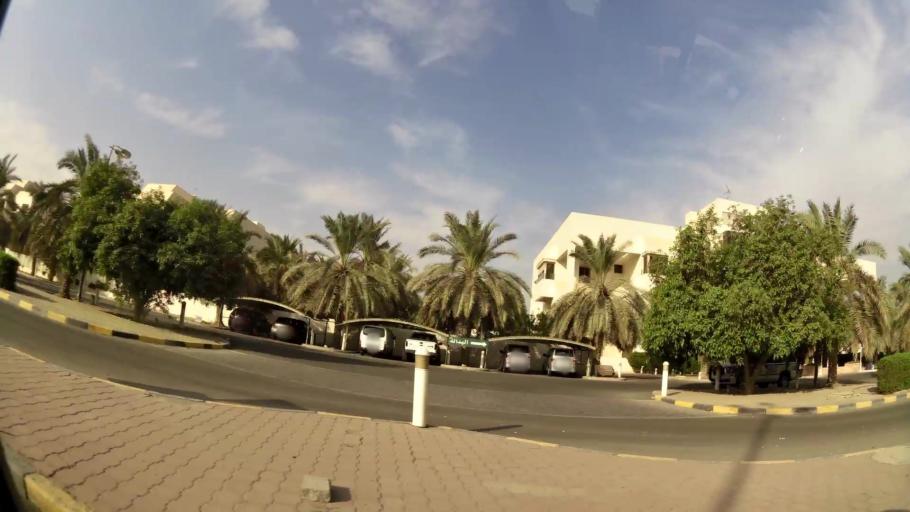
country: KW
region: Muhafazat Hawalli
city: Salwa
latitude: 29.2830
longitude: 48.0870
